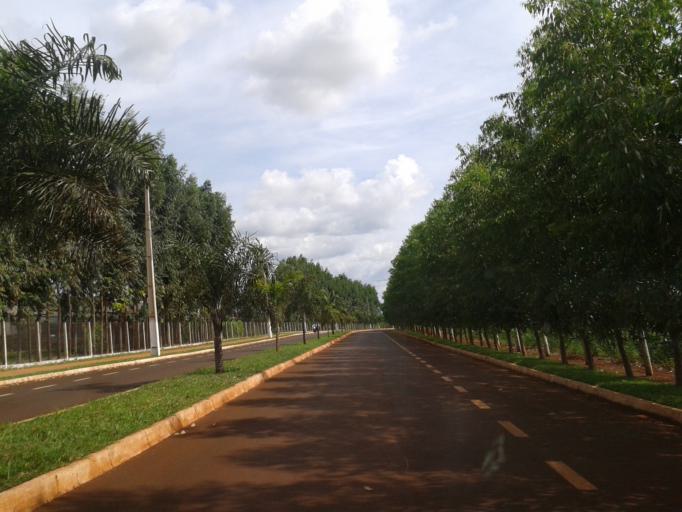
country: BR
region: Minas Gerais
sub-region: Centralina
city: Centralina
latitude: -18.5732
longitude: -49.1949
